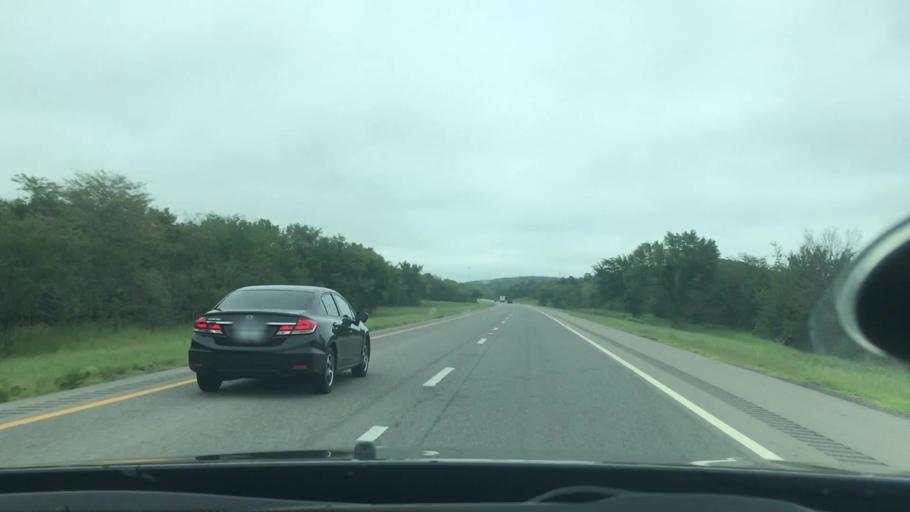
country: US
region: Oklahoma
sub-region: Muskogee County
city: Warner
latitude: 35.4562
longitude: -95.4057
